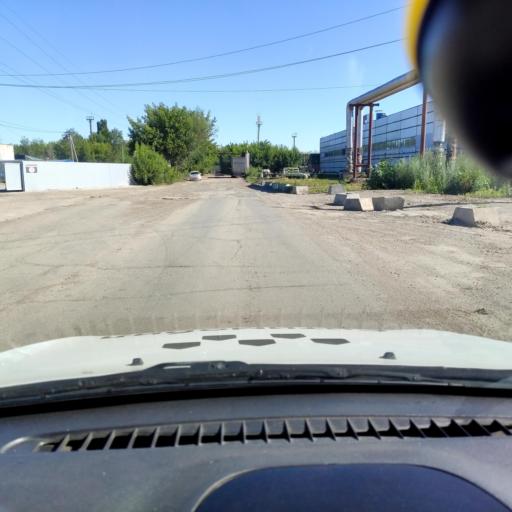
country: RU
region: Samara
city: Tol'yatti
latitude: 53.5866
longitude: 49.2576
